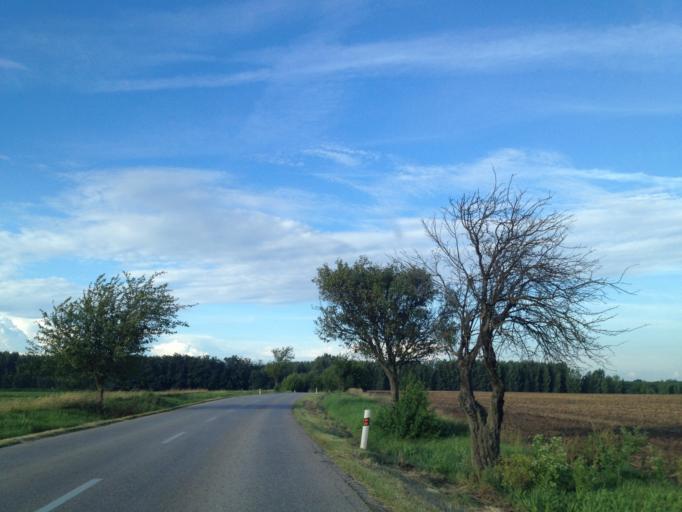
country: SK
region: Nitriansky
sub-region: Okres Komarno
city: Hurbanovo
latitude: 47.8216
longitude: 18.2292
